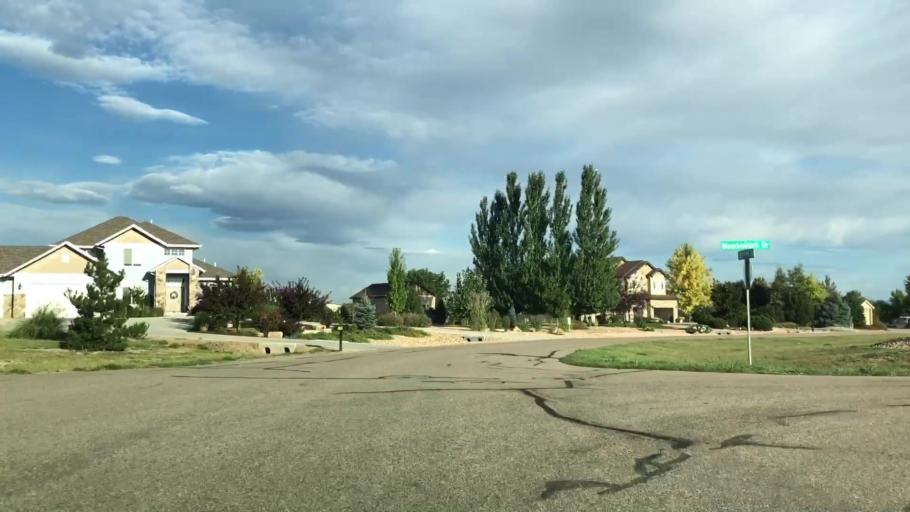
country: US
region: Colorado
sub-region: Weld County
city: Windsor
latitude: 40.4378
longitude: -104.9612
